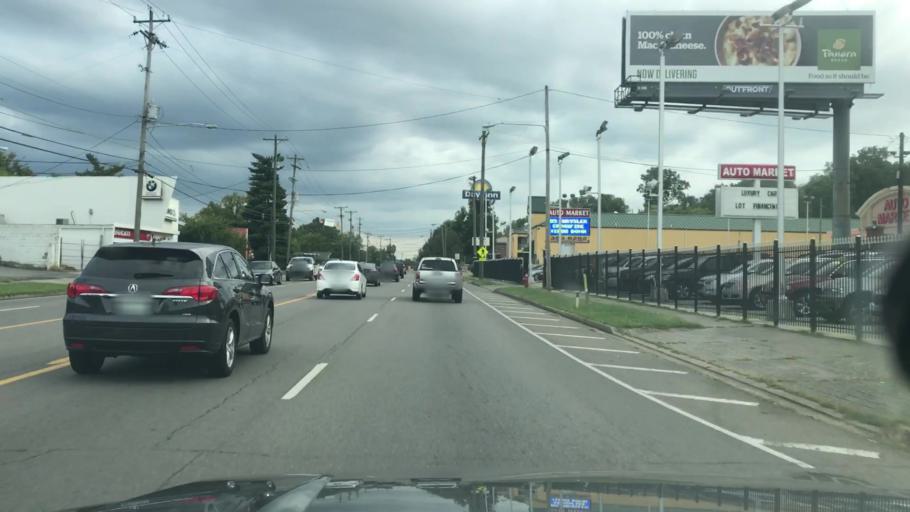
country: US
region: Tennessee
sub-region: Davidson County
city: Belle Meade
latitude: 36.1449
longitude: -86.8580
